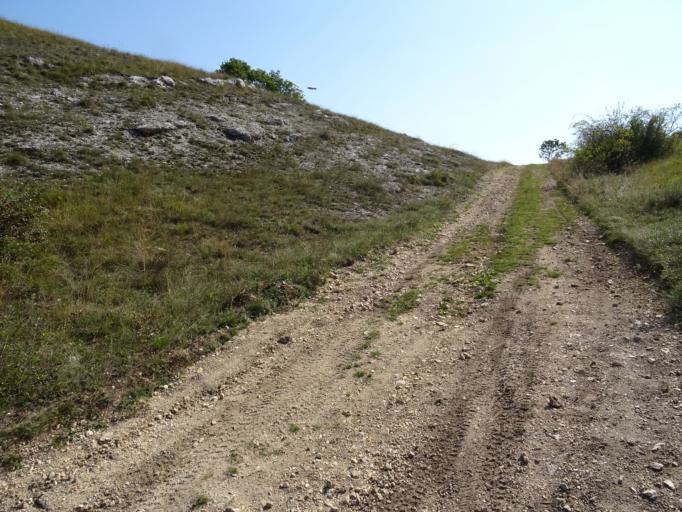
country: HU
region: Fejer
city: Zamoly
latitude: 47.3840
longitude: 18.3861
